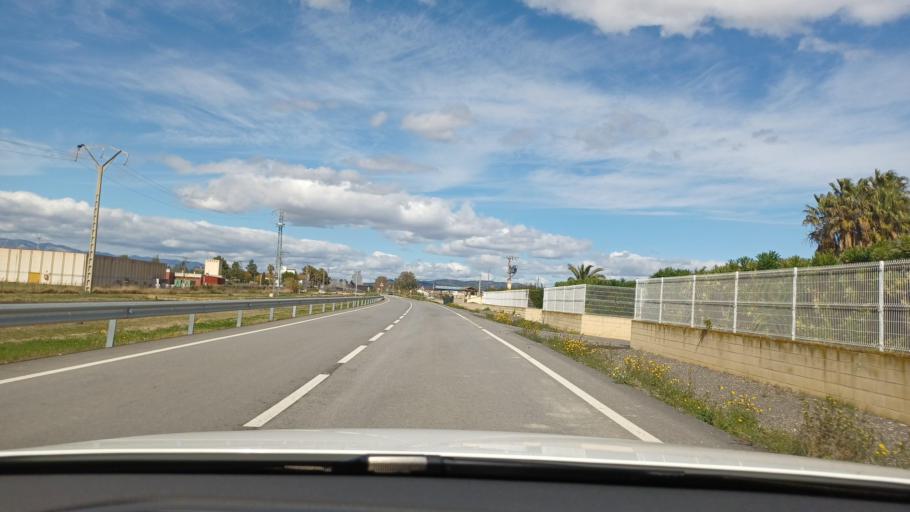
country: ES
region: Catalonia
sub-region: Provincia de Tarragona
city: Amposta
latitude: 40.7004
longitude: 0.5885
